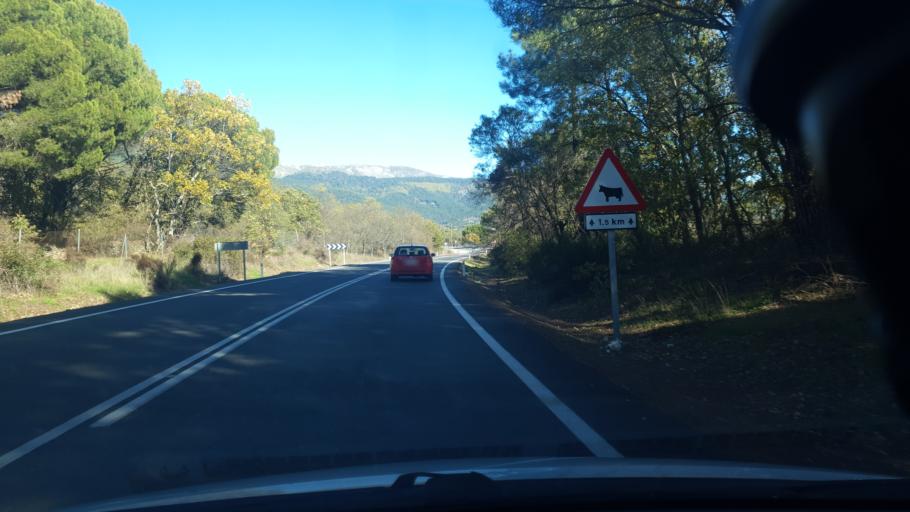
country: ES
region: Castille and Leon
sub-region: Provincia de Avila
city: Piedralaves
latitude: 40.2918
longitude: -4.7239
